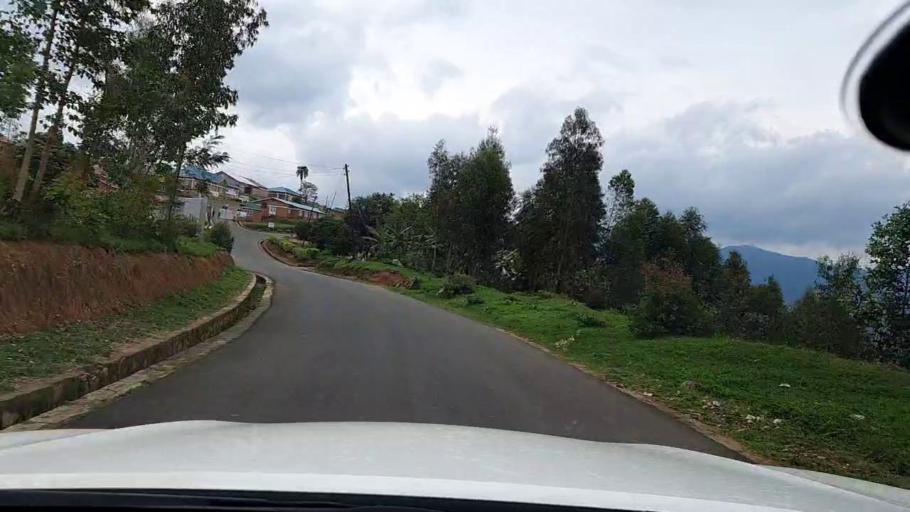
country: RW
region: Western Province
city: Kibuye
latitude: -2.1795
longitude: 29.2907
